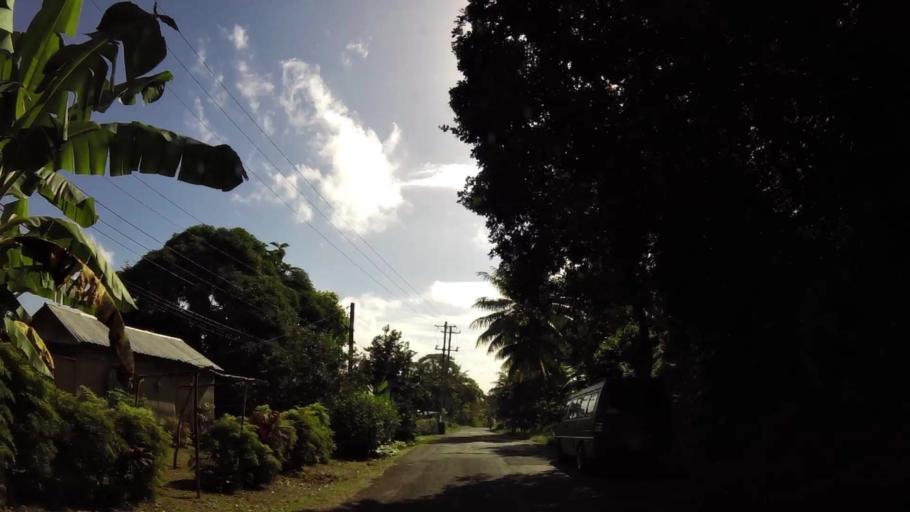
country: DM
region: Saint David
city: Castle Bruce
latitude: 15.4799
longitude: -61.2520
